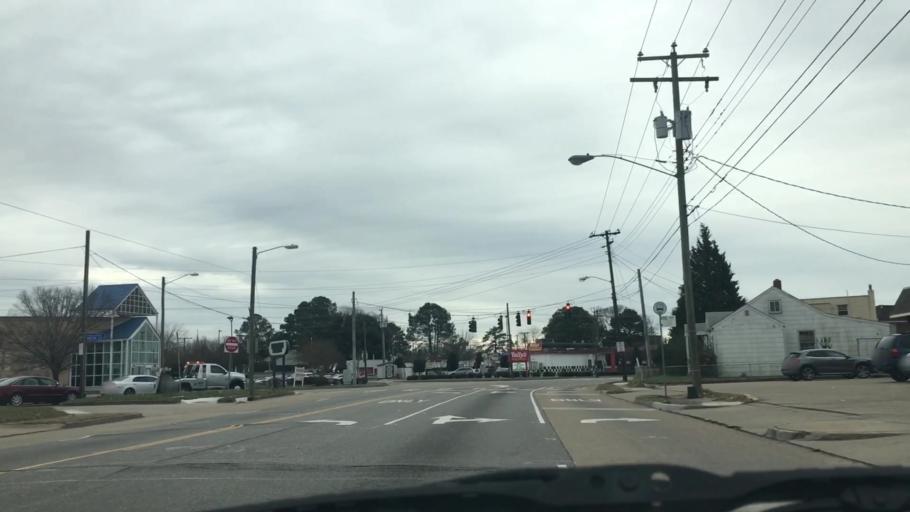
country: US
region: Virginia
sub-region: City of Norfolk
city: Norfolk
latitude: 36.8718
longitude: -76.2322
